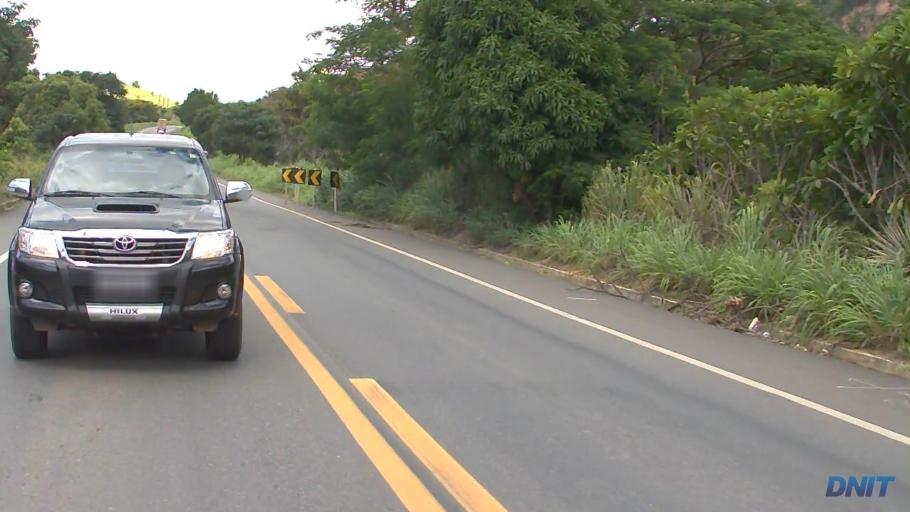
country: BR
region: Minas Gerais
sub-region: Governador Valadares
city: Governador Valadares
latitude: -18.9521
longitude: -42.0720
